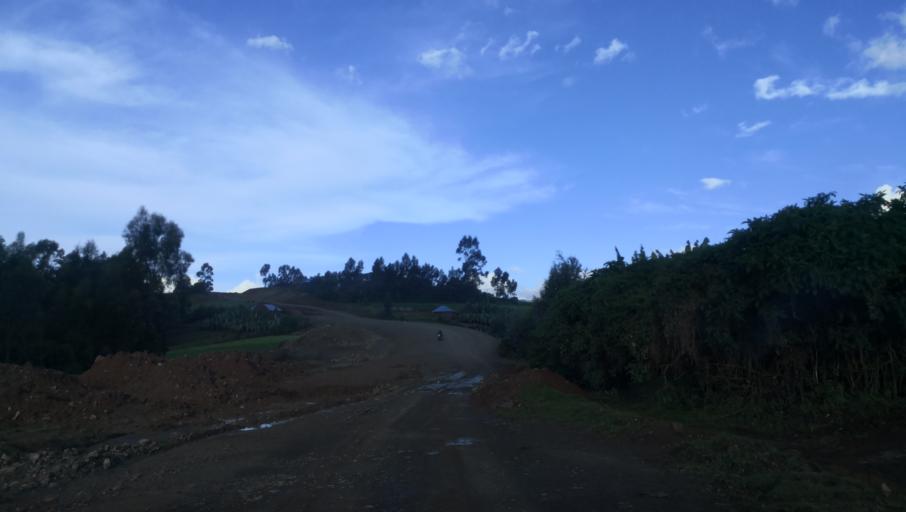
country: ET
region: Southern Nations, Nationalities, and People's Region
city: Butajira
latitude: 8.3975
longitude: 38.3138
